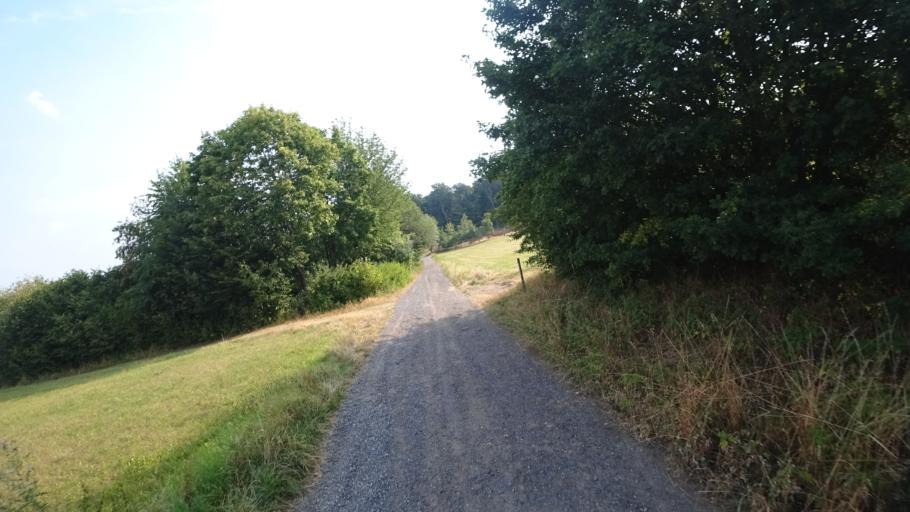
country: DE
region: Rheinland-Pfalz
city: Hilgert
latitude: 50.4620
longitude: 7.6908
